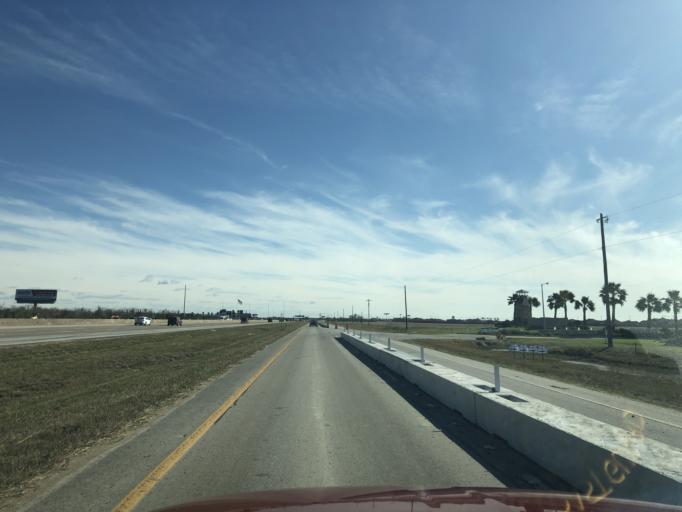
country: US
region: Texas
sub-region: Galveston County
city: Dickinson
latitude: 29.4176
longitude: -95.0482
